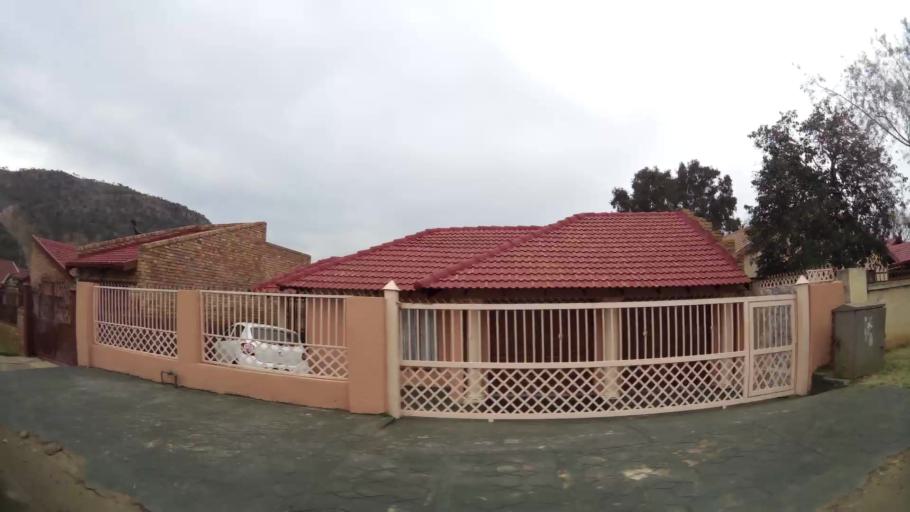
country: ZA
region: Gauteng
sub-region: City of Tshwane Metropolitan Municipality
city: Cullinan
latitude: -25.7013
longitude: 28.3566
